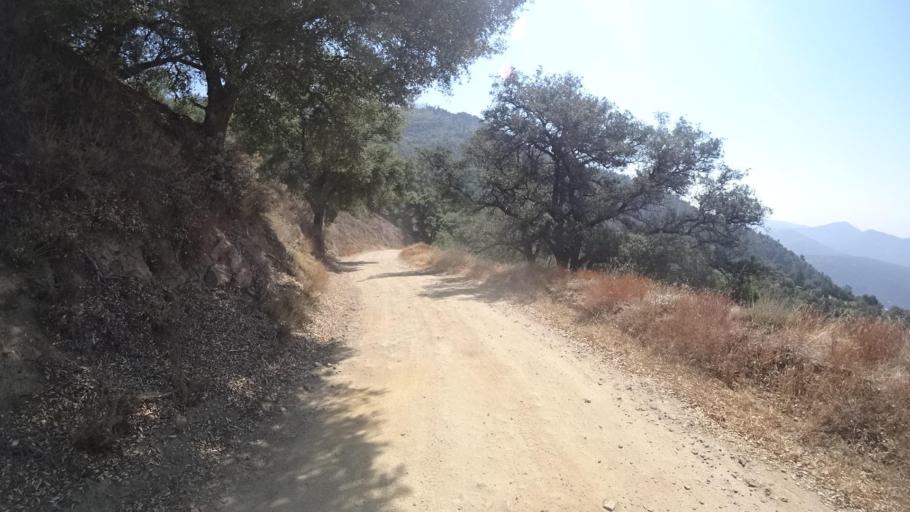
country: US
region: California
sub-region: Riverside County
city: Aguanga
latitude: 33.3342
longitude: -116.9413
